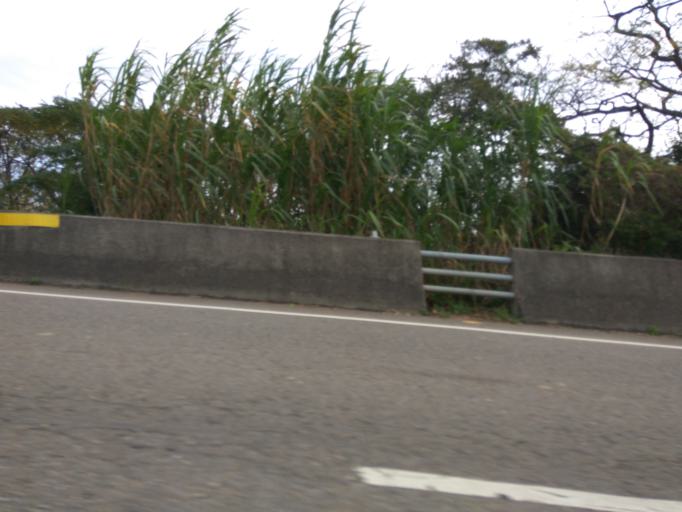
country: TW
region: Taiwan
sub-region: Hsinchu
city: Zhubei
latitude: 24.9538
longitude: 121.0118
